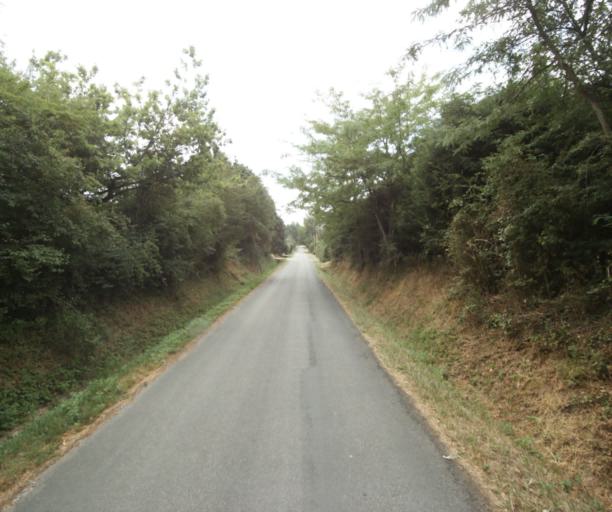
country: FR
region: Midi-Pyrenees
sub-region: Departement de la Haute-Garonne
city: Revel
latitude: 43.4489
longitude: 1.9977
